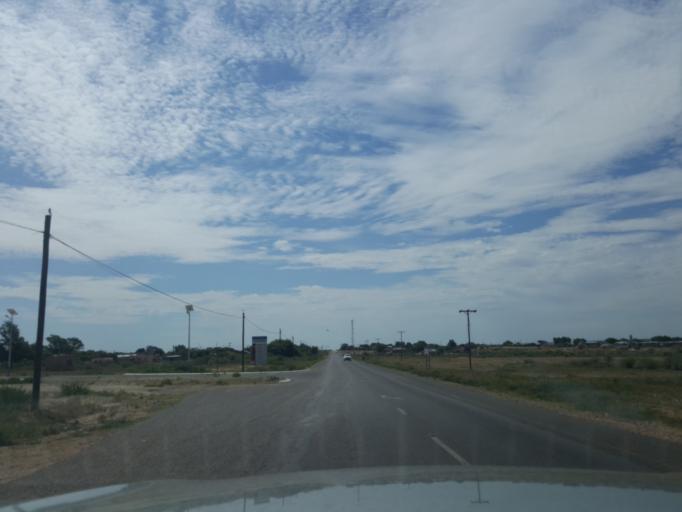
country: BW
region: Kweneng
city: Letlhakeng
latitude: -24.1117
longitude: 25.0354
